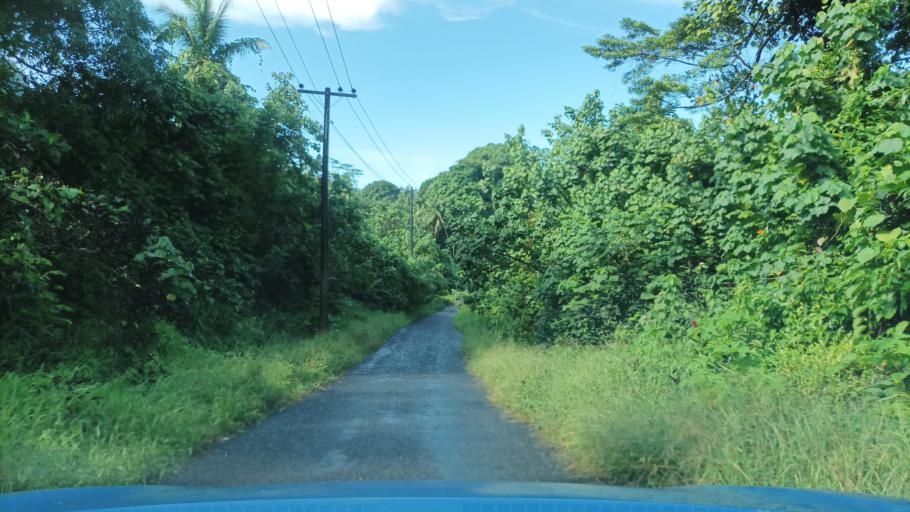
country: FM
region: Pohnpei
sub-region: Sokehs Municipality
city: Palikir - National Government Center
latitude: 6.9339
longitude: 158.1849
